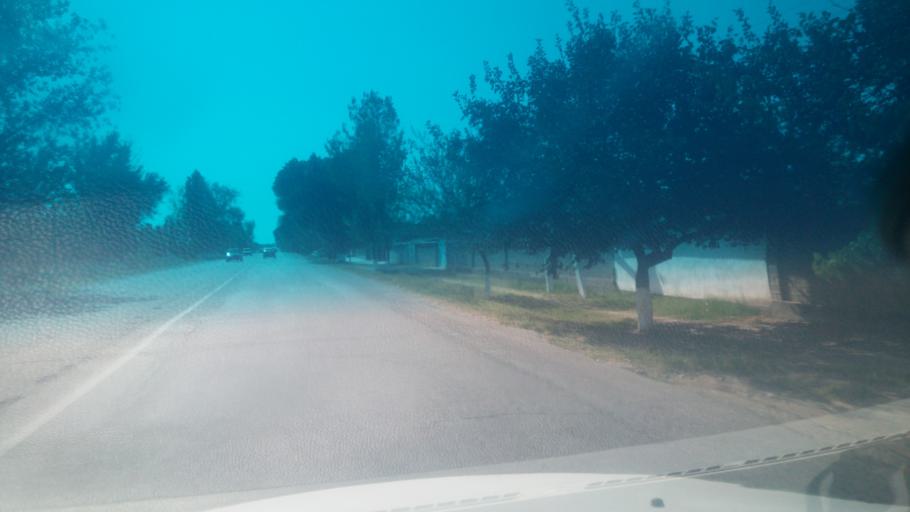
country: UZ
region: Sirdaryo
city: Sirdaryo
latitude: 40.8127
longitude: 68.6752
